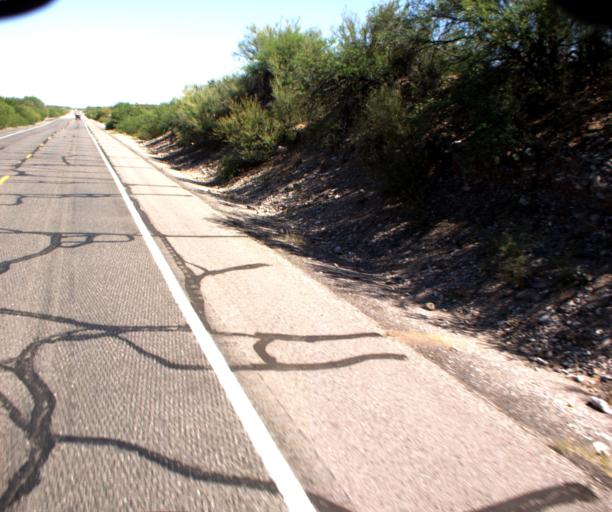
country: US
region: Arizona
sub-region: Pinal County
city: Mammoth
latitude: 32.7987
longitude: -110.6779
